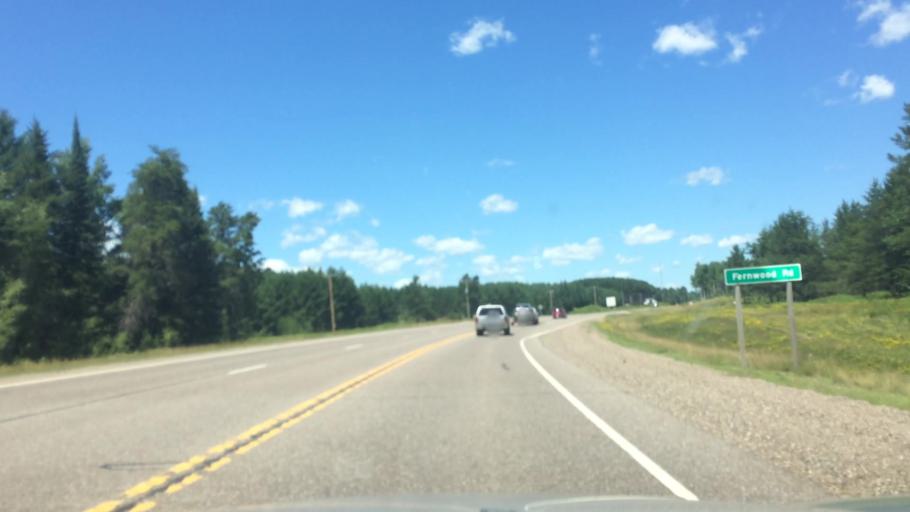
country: US
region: Wisconsin
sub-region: Lincoln County
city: Tomahawk
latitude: 45.6649
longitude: -89.7136
